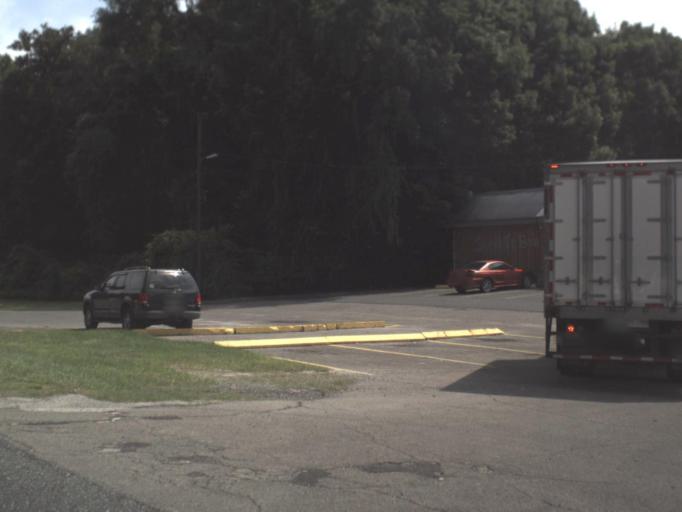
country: US
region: Florida
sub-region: Alachua County
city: High Springs
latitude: 29.8578
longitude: -82.6085
